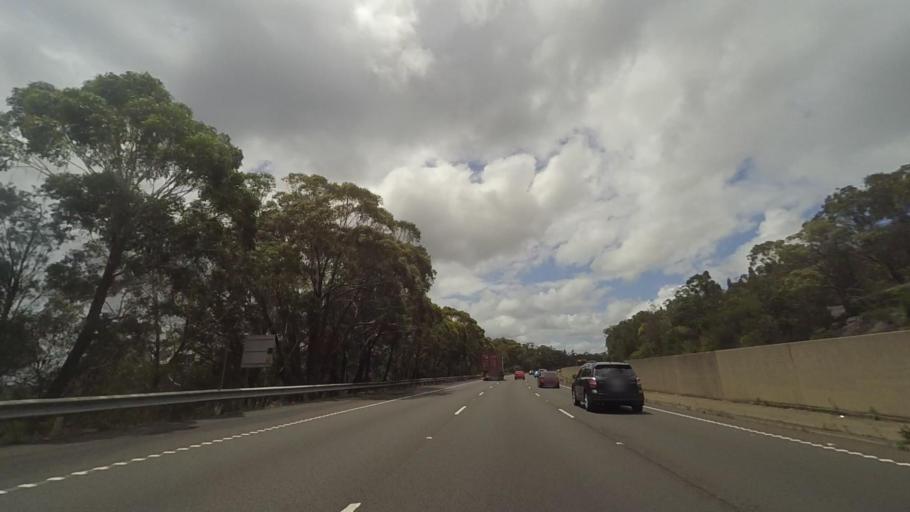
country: AU
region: New South Wales
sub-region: Gosford Shire
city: Point Clare
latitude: -33.4402
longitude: 151.2184
